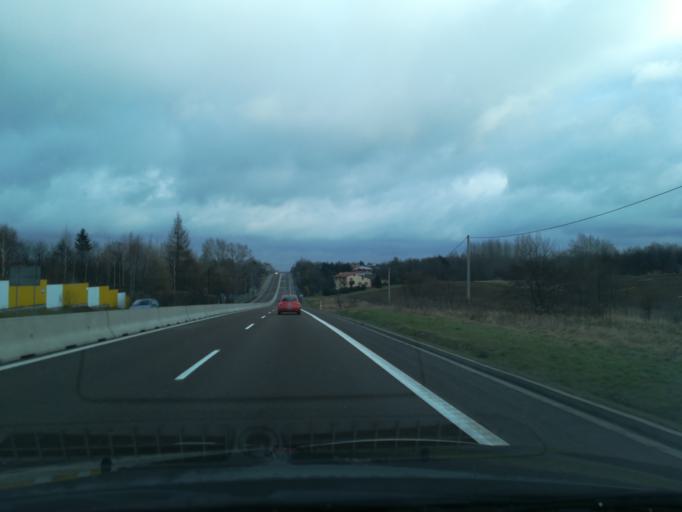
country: PL
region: Subcarpathian Voivodeship
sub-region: Powiat lancucki
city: Krzemienica
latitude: 50.0519
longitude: 22.1951
